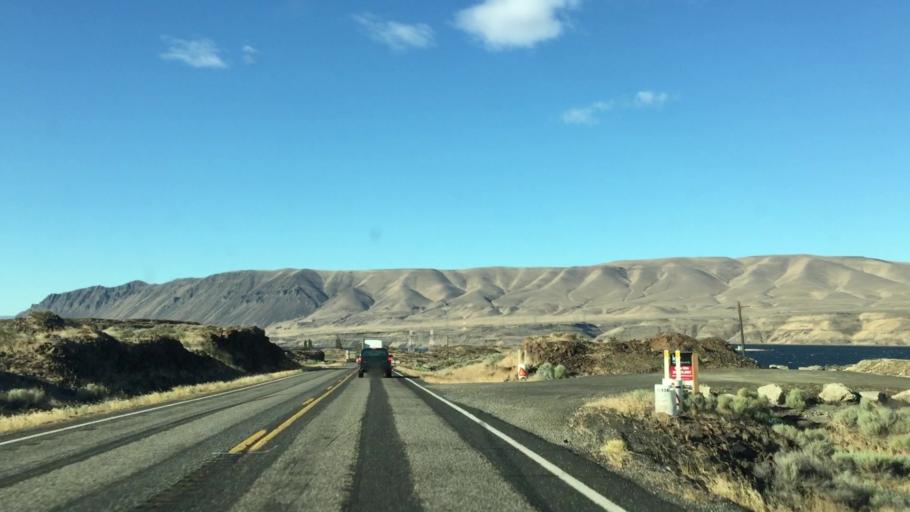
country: US
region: Washington
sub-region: Grant County
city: Mattawa
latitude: 46.8927
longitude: -119.9537
